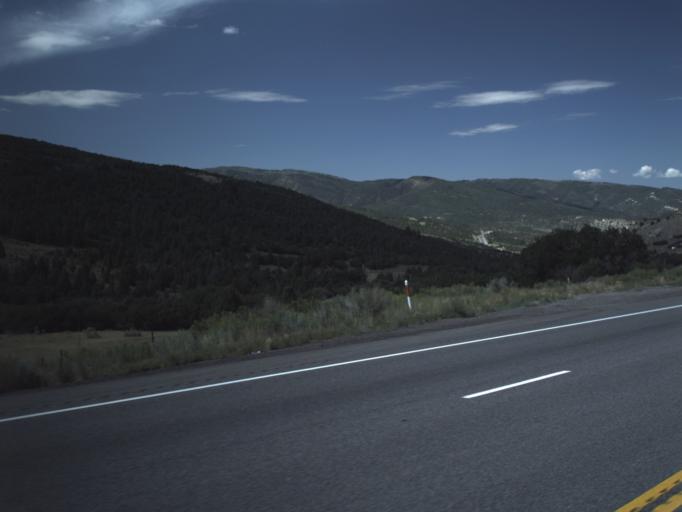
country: US
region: Utah
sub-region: Carbon County
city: Helper
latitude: 39.9363
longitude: -111.1344
